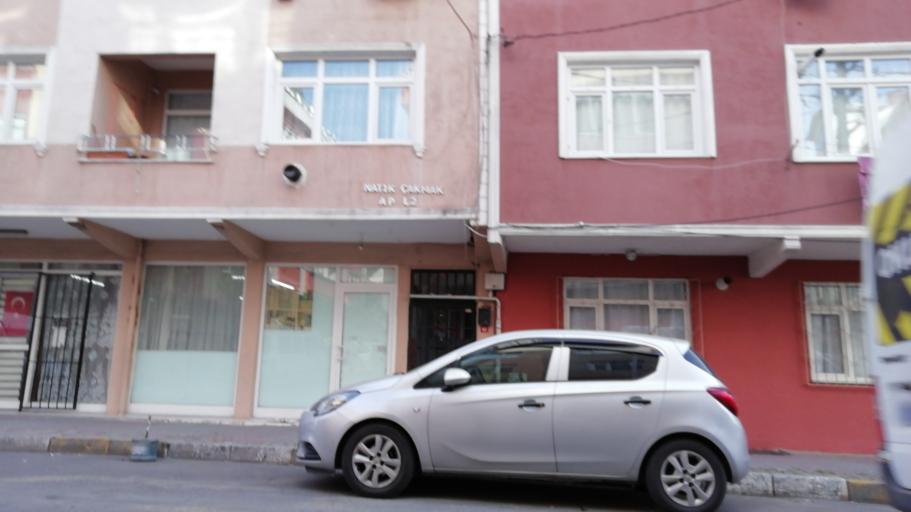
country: TR
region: Istanbul
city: Bagcilar
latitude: 41.0275
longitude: 28.8387
